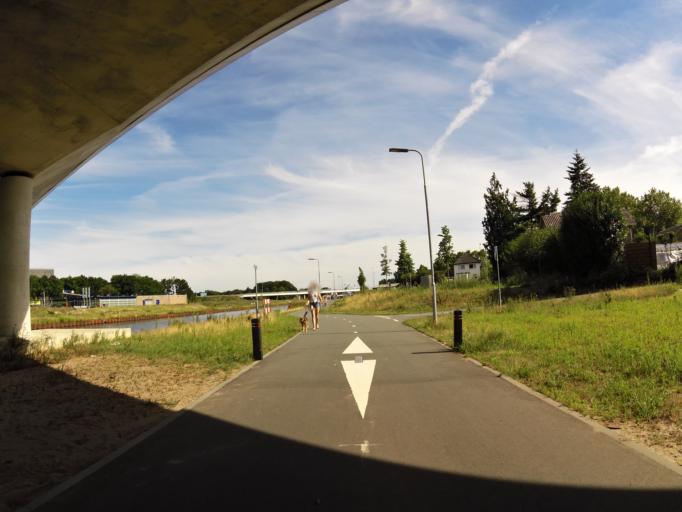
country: NL
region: North Brabant
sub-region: Gemeente 's-Hertogenbosch
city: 's-Hertogenbosch
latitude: 51.7033
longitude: 5.3551
